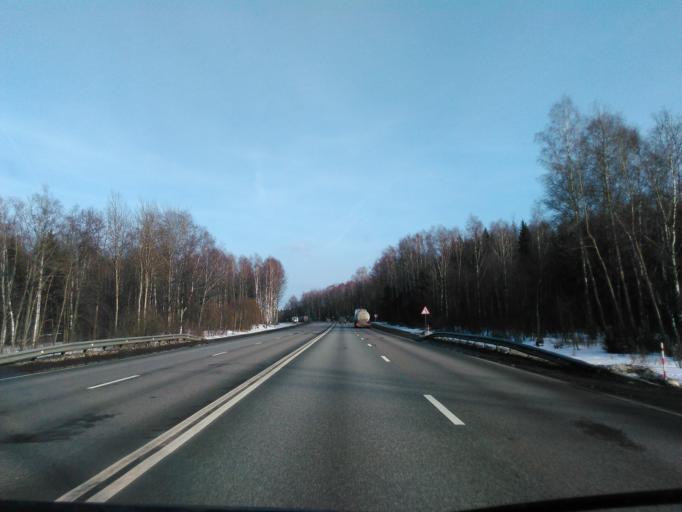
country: RU
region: Smolensk
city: Vyaz'ma
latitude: 55.1875
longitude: 34.0545
